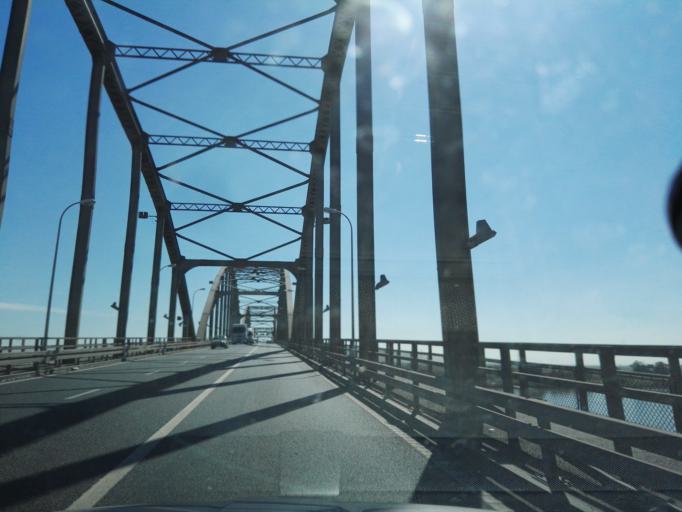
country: PT
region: Lisbon
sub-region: Vila Franca de Xira
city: Vila Franca de Xira
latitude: 38.9576
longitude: -8.9806
